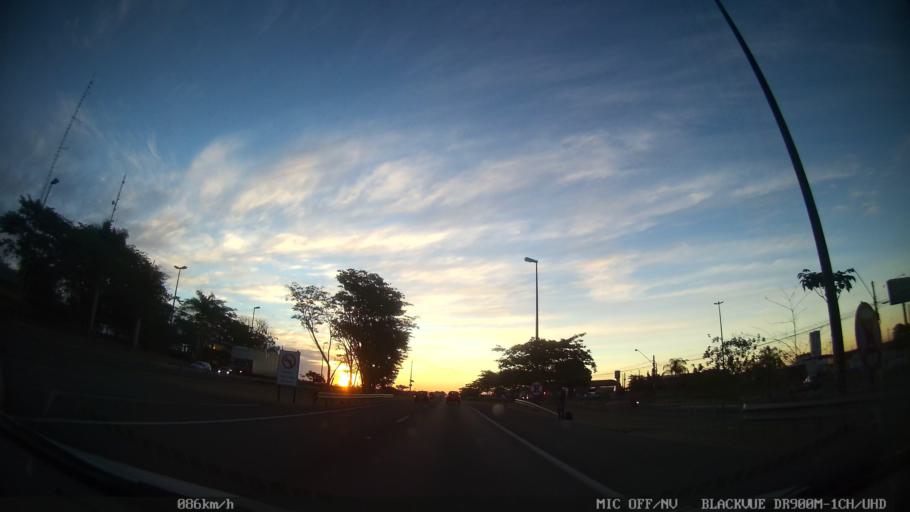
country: BR
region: Sao Paulo
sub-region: Catanduva
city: Catanduva
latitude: -21.1510
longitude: -48.9979
